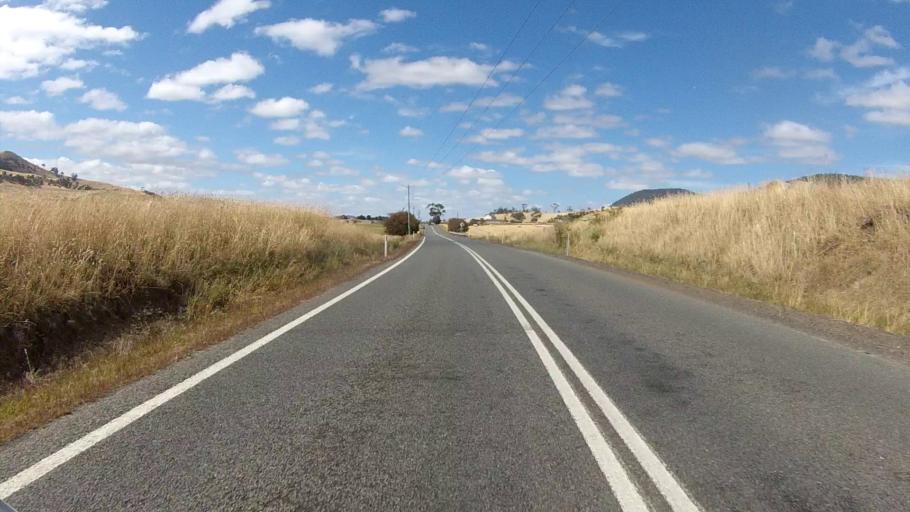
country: AU
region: Tasmania
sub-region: Brighton
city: Bridgewater
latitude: -42.5877
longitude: 147.4084
